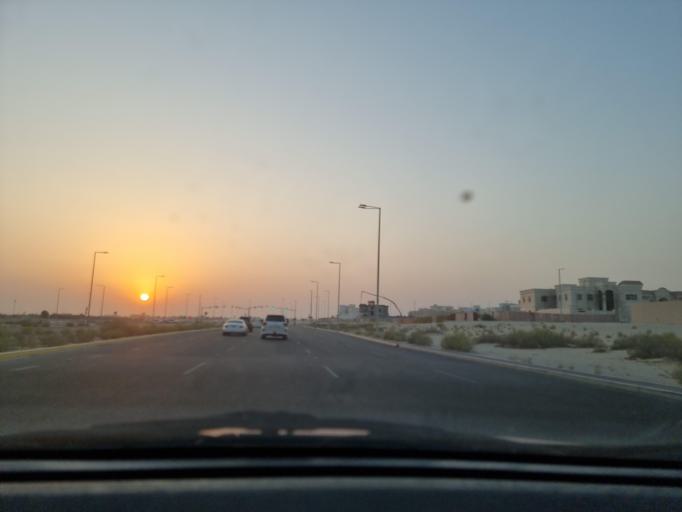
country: AE
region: Abu Dhabi
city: Abu Dhabi
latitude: 24.3729
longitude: 54.7420
